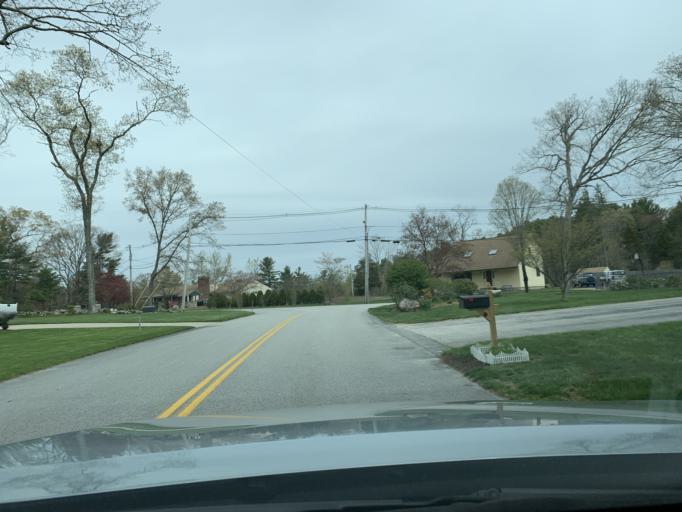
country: US
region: Rhode Island
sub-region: Washington County
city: North Kingstown
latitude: 41.6032
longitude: -71.4855
